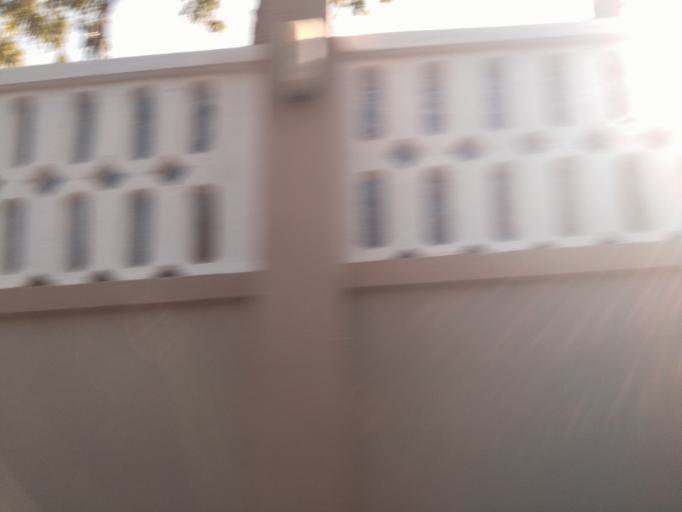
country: TZ
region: Dar es Salaam
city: Magomeni
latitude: -6.7662
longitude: 39.2542
